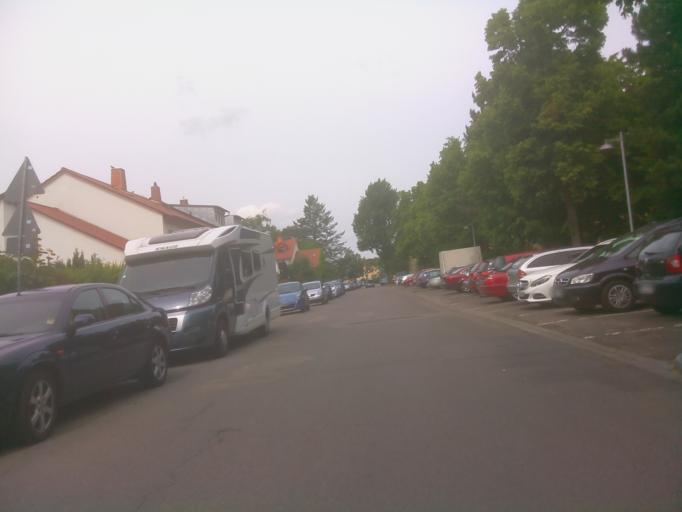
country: DE
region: Baden-Wuerttemberg
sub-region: Karlsruhe Region
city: Mannheim
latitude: 49.5352
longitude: 8.4904
